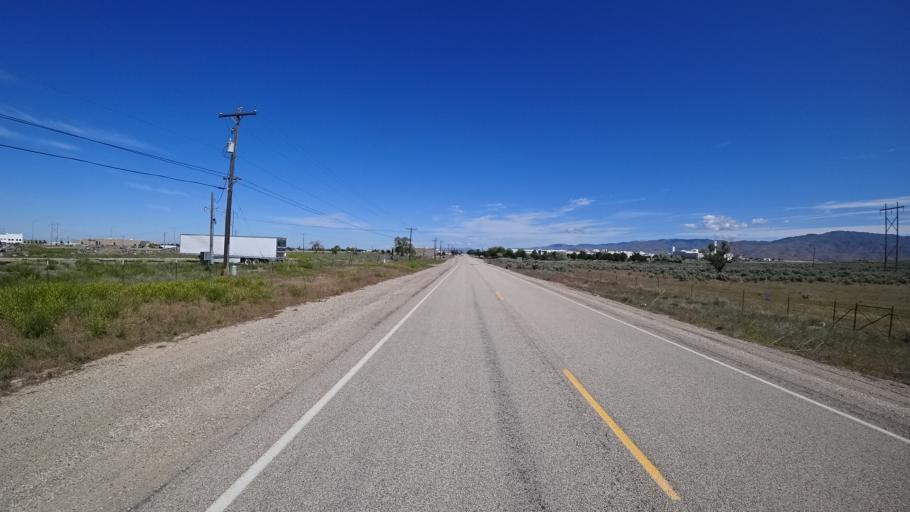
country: US
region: Idaho
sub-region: Ada County
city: Boise
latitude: 43.5152
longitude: -116.1442
